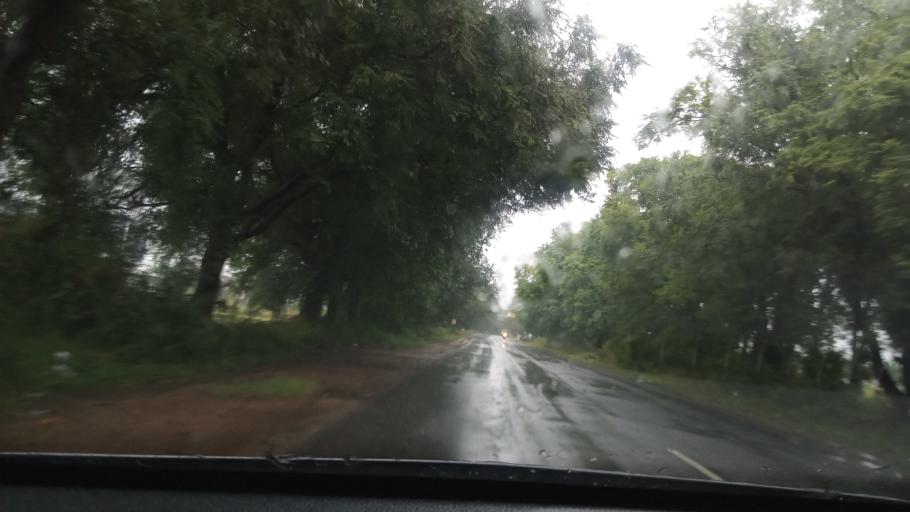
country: IN
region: Tamil Nadu
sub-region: Vellore
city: Walajapet
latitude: 12.8477
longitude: 79.3926
